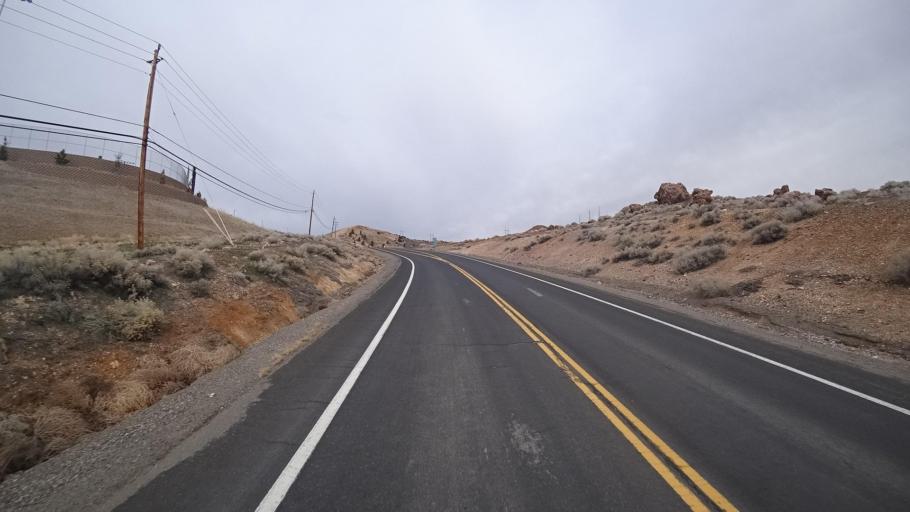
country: US
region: Nevada
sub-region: Washoe County
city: Sun Valley
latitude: 39.5739
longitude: -119.7898
